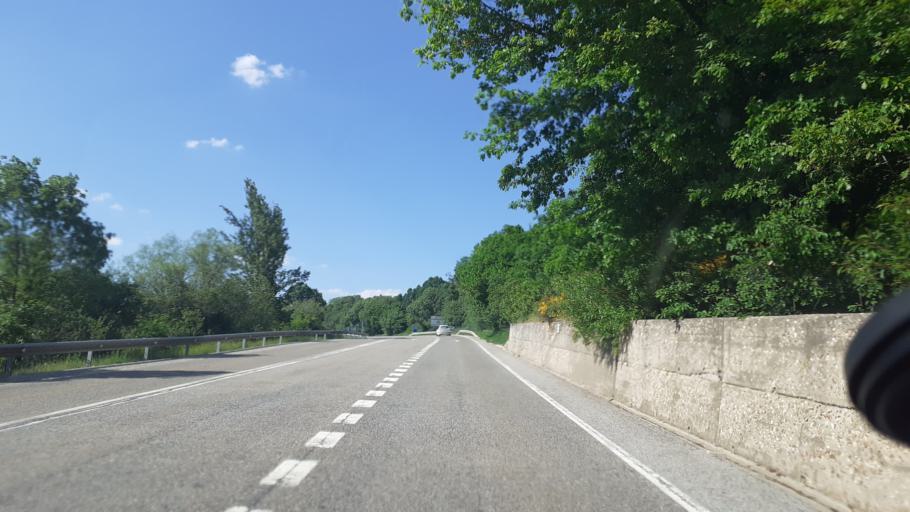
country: ES
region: Madrid
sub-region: Provincia de Madrid
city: Somosierra
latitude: 41.1287
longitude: -3.5811
